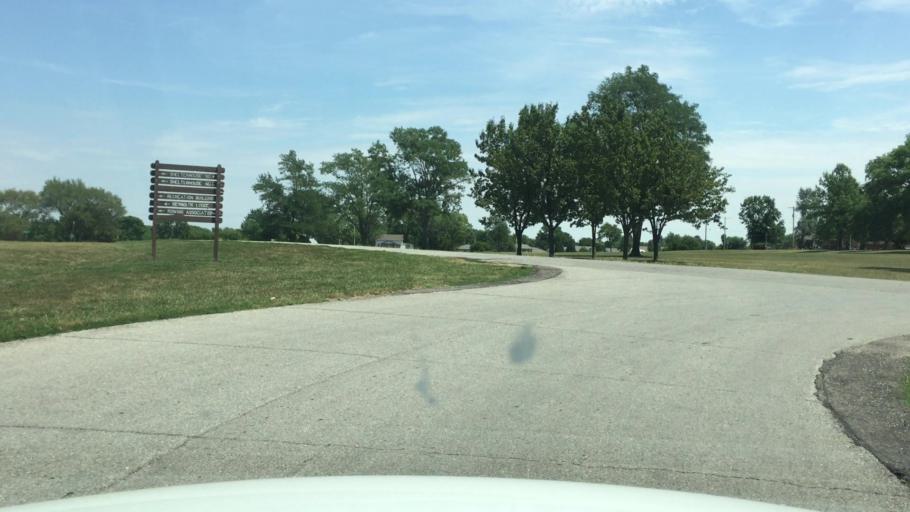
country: US
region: Kansas
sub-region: Shawnee County
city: Topeka
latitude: 39.0060
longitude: -95.6178
